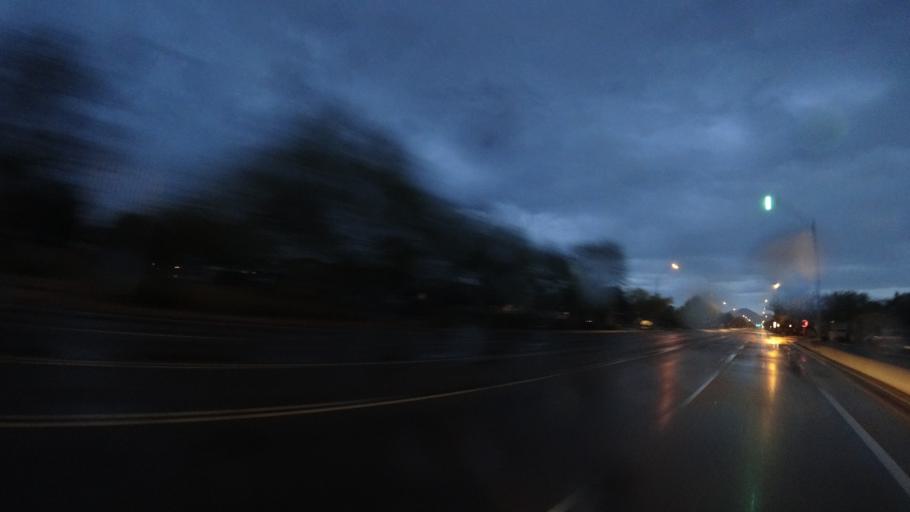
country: US
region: Arizona
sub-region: Maricopa County
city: Paradise Valley
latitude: 33.6552
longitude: -111.9871
